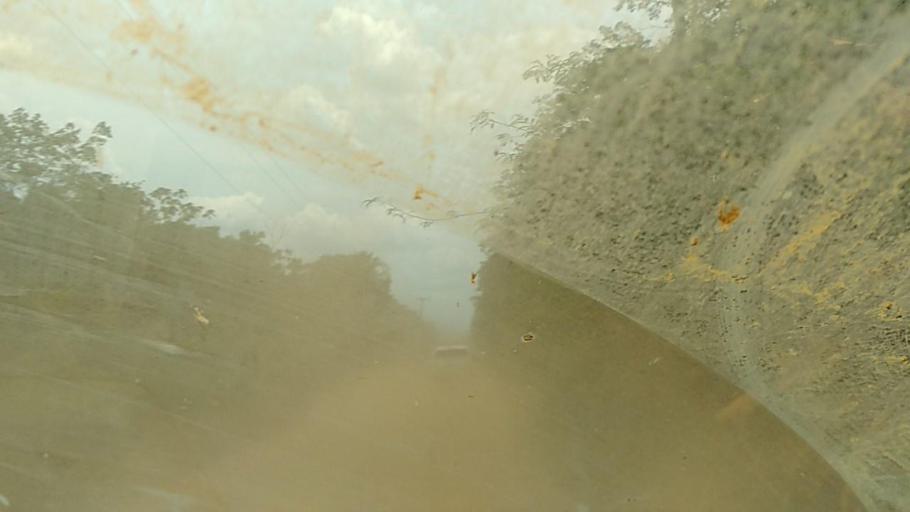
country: BR
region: Rondonia
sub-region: Porto Velho
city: Porto Velho
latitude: -8.9570
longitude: -64.3207
